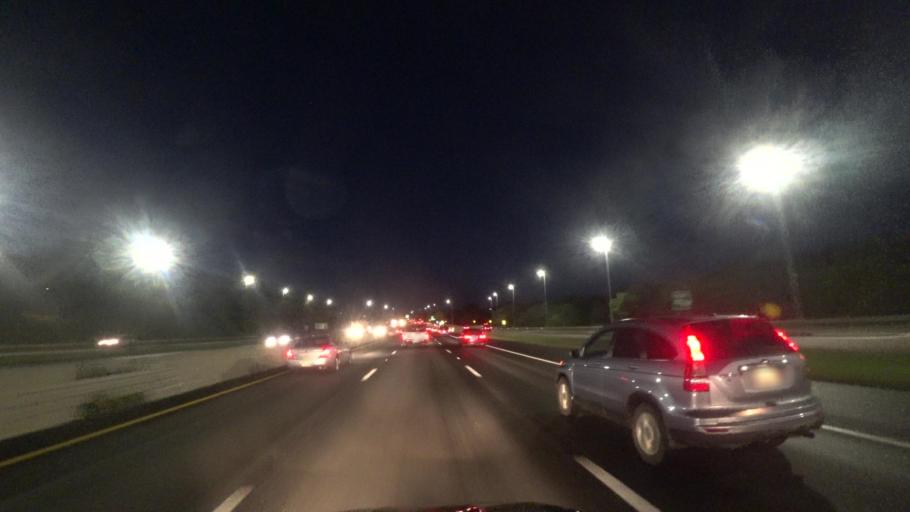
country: US
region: Massachusetts
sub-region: Essex County
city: North Andover
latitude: 42.7019
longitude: -71.1406
